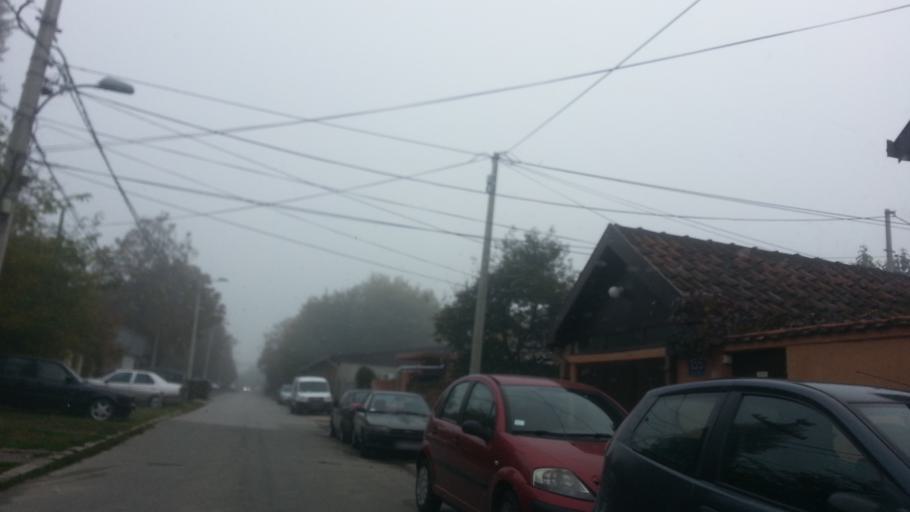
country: RS
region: Central Serbia
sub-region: Belgrade
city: Zemun
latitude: 44.8569
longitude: 20.3865
